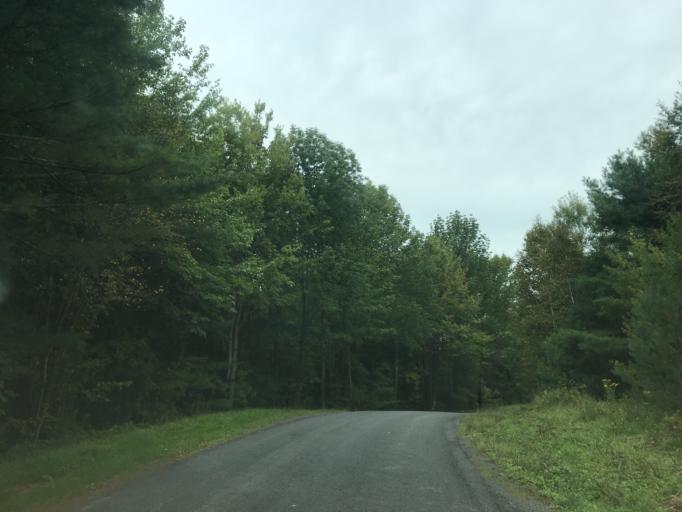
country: US
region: New York
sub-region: Otsego County
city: Worcester
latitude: 42.5345
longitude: -74.6633
